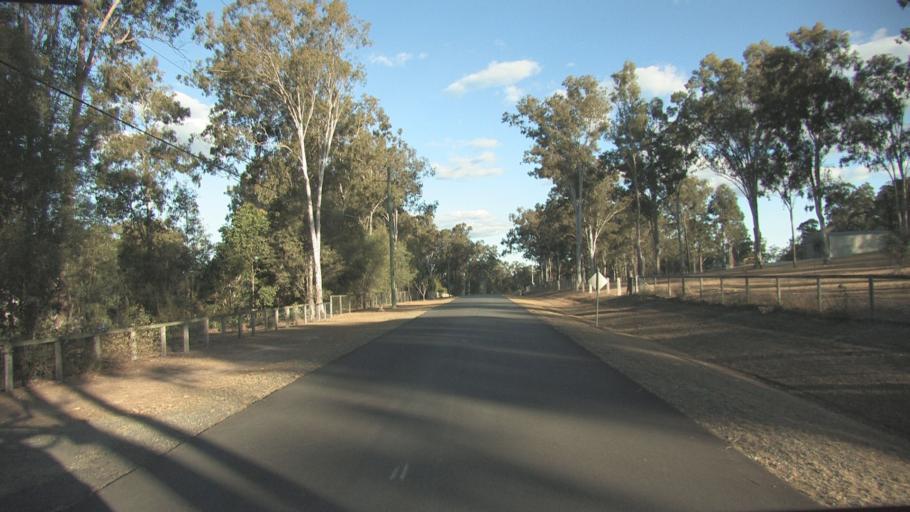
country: AU
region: Queensland
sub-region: Logan
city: Cedar Vale
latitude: -27.8549
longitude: 153.0977
